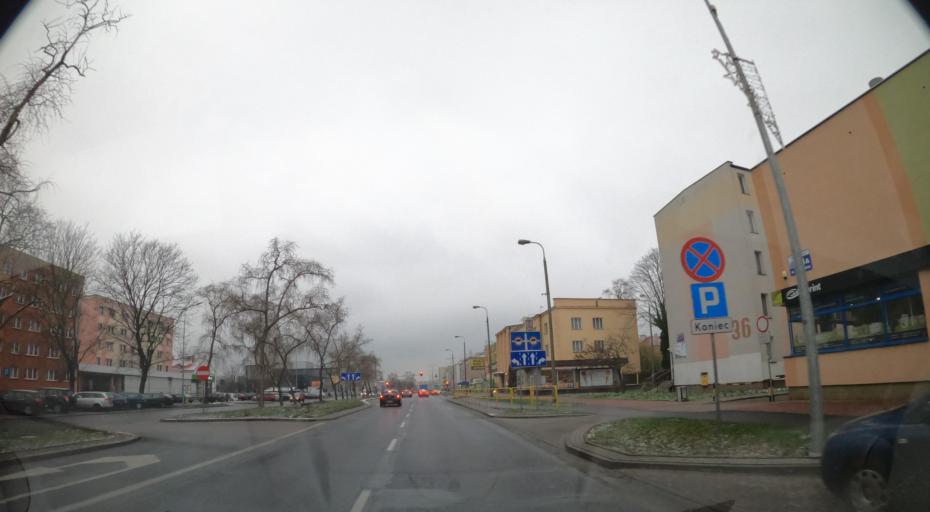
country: PL
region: Masovian Voivodeship
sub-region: Plock
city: Plock
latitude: 52.5489
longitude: 19.6962
